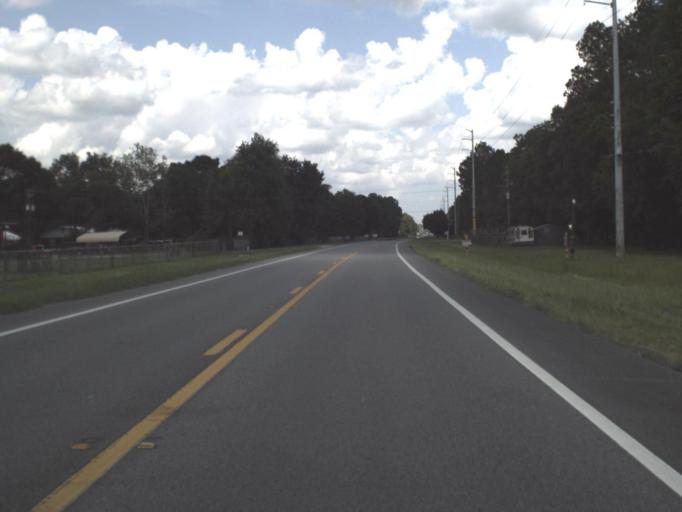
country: US
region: Florida
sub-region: Bradford County
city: Starke
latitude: 29.9537
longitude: -82.0751
